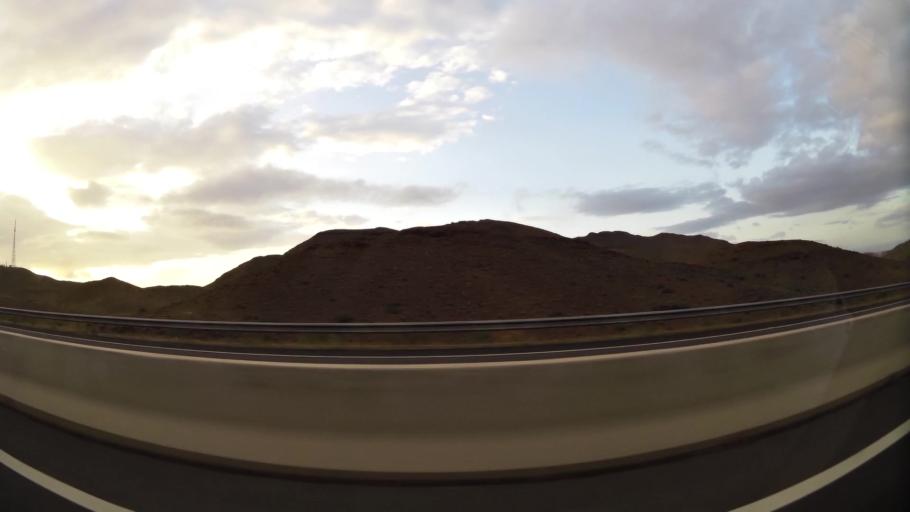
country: MA
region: Oriental
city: Taourirt
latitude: 34.4657
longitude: -3.0101
